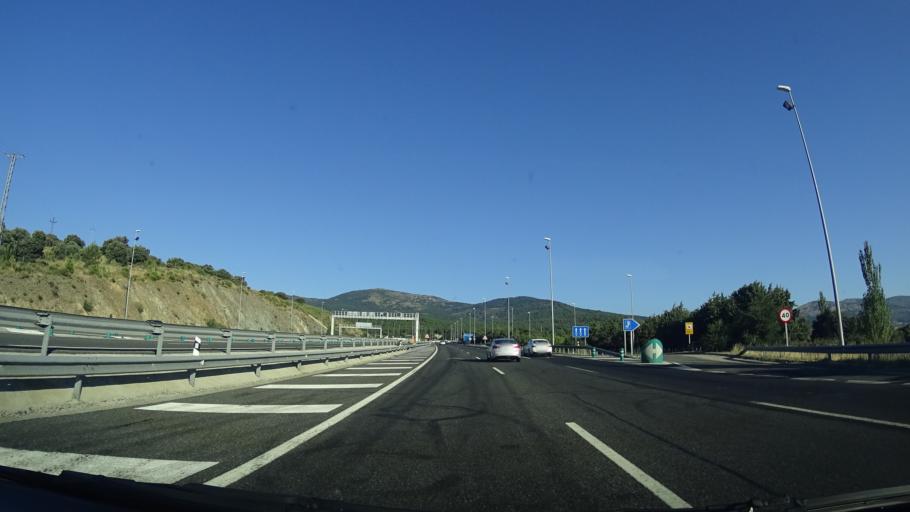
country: ES
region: Madrid
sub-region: Provincia de Madrid
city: Guadarrama
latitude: 40.6686
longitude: -4.1046
